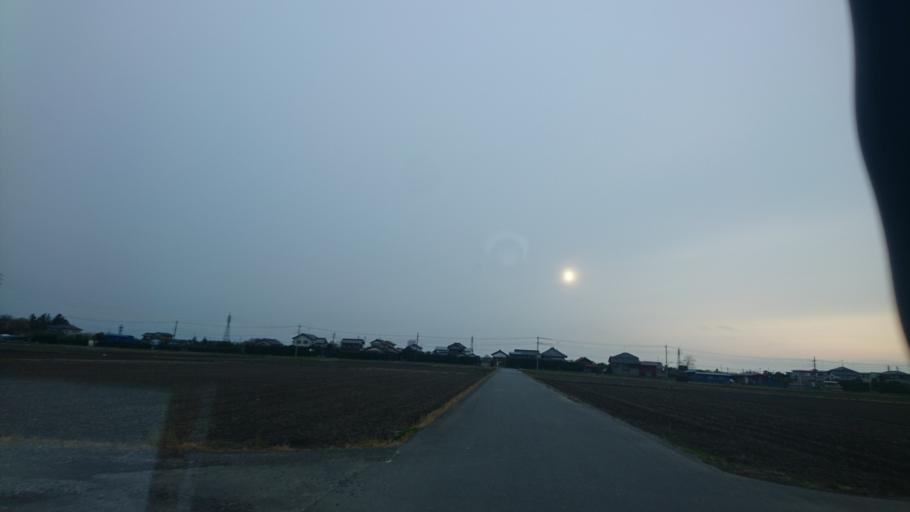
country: JP
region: Ibaraki
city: Mitsukaido
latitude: 36.0342
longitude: 140.0092
